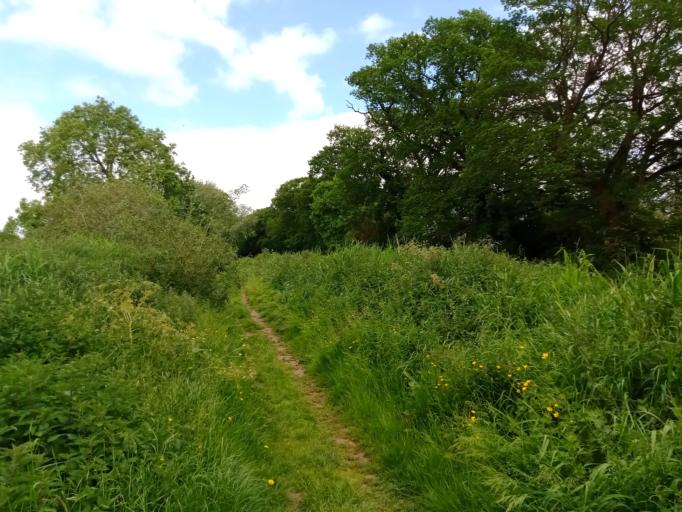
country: IE
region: Leinster
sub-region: County Carlow
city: Carlow
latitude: 52.8124
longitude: -6.9588
